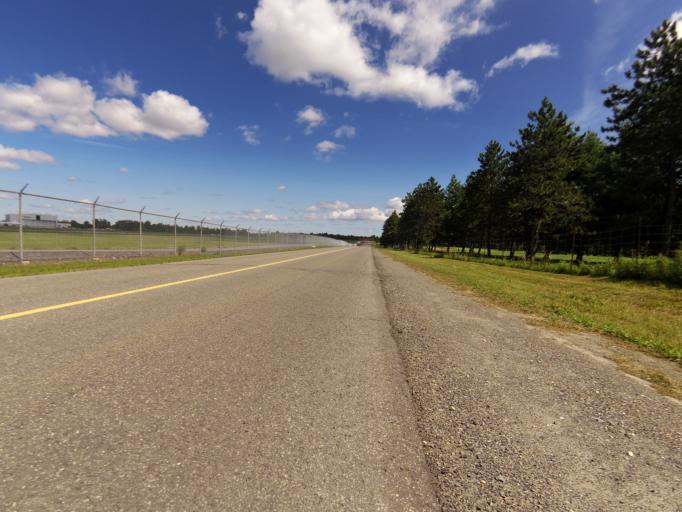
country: CA
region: Ontario
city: Ottawa
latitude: 45.3202
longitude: -75.6475
